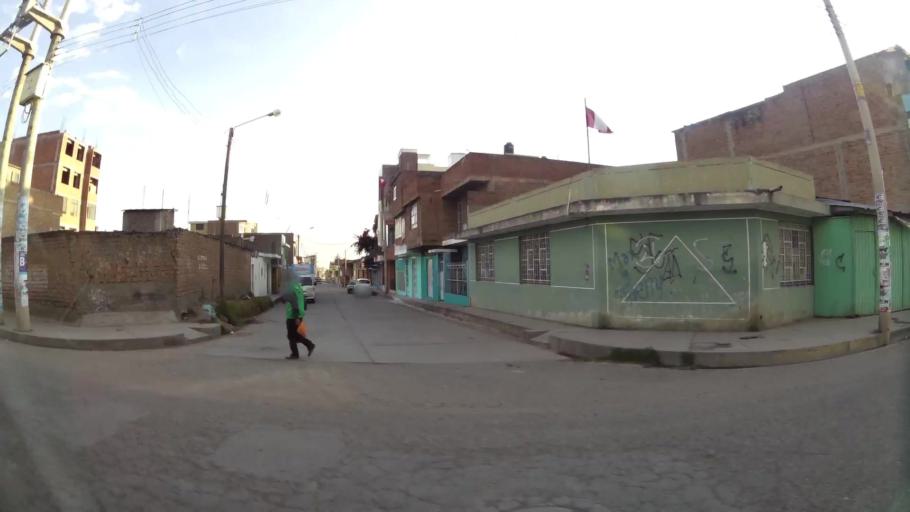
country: PE
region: Junin
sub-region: Provincia de Huancayo
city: El Tambo
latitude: -12.0532
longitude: -75.2139
